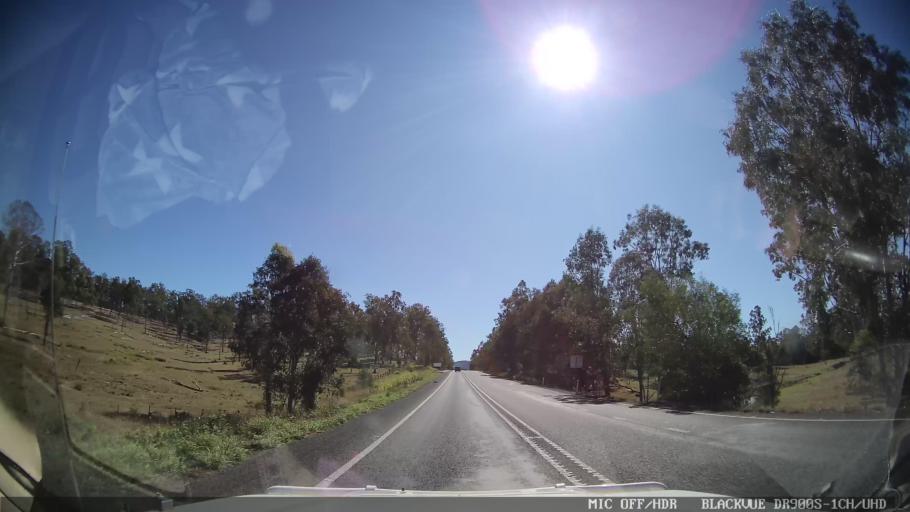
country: AU
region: Queensland
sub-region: Gympie Regional Council
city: Gympie
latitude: -26.0027
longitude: 152.5666
